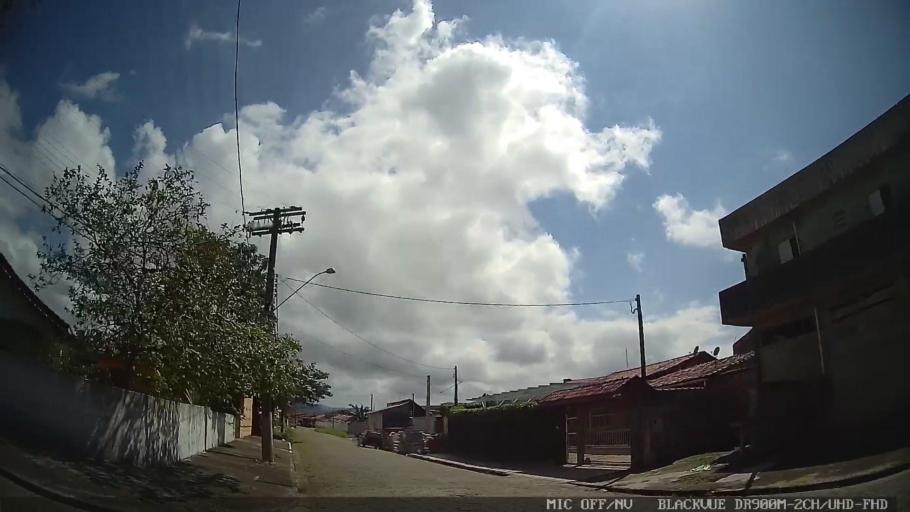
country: BR
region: Sao Paulo
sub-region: Peruibe
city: Peruibe
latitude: -24.3086
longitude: -47.0044
